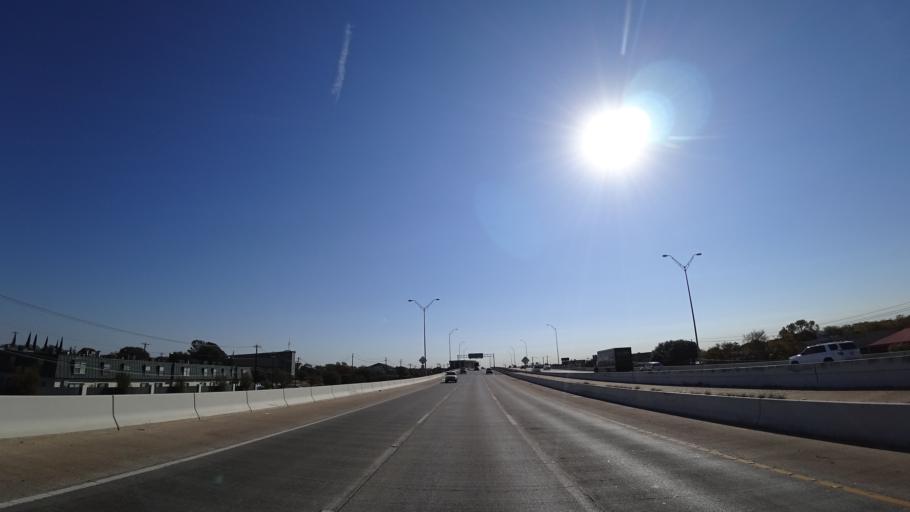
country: US
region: Texas
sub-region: Travis County
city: Austin
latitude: 30.3453
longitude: -97.7075
